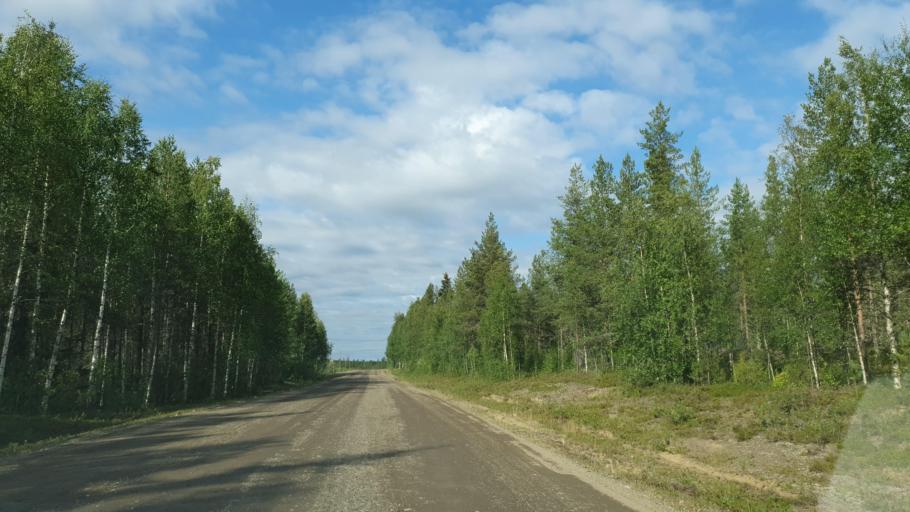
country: FI
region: Lapland
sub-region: Pohjois-Lappi
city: Sodankylae
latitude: 67.5255
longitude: 26.0054
